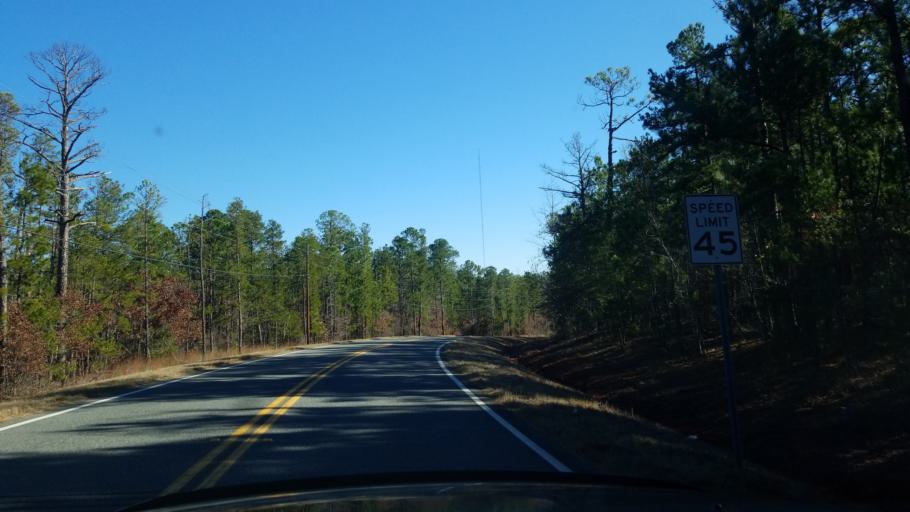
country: US
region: Georgia
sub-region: Meriwether County
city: Manchester
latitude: 32.8493
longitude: -84.6981
